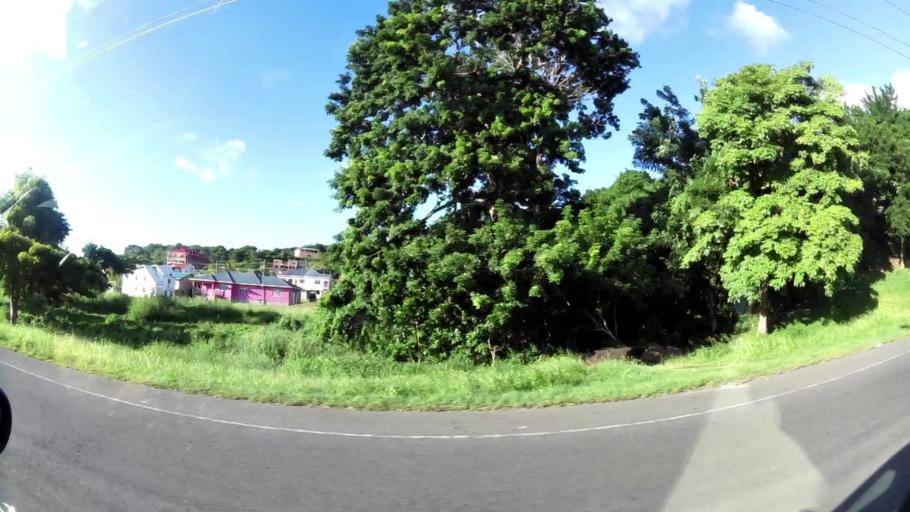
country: TT
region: Tobago
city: Scarborough
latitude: 11.1794
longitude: -60.7082
